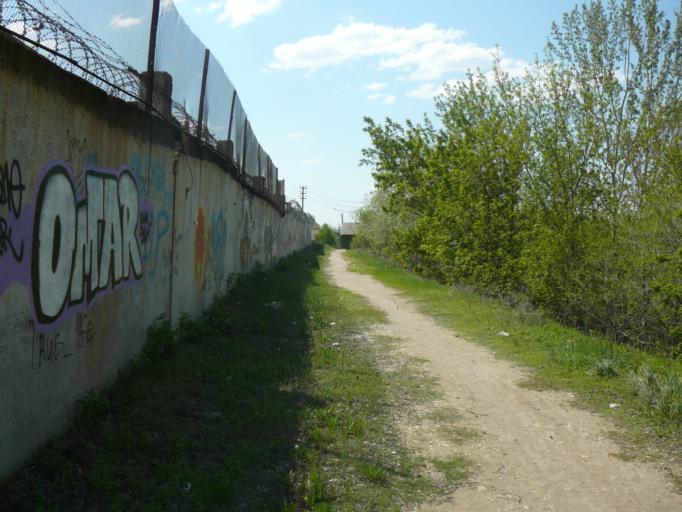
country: RU
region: Saratov
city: Engel's
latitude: 51.4906
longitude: 46.0963
